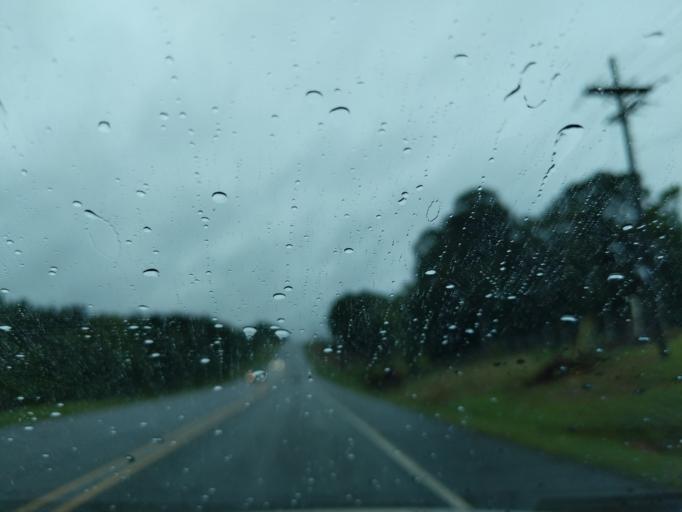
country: US
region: Louisiana
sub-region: Webster Parish
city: Minden
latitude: 32.6089
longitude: -93.2498
